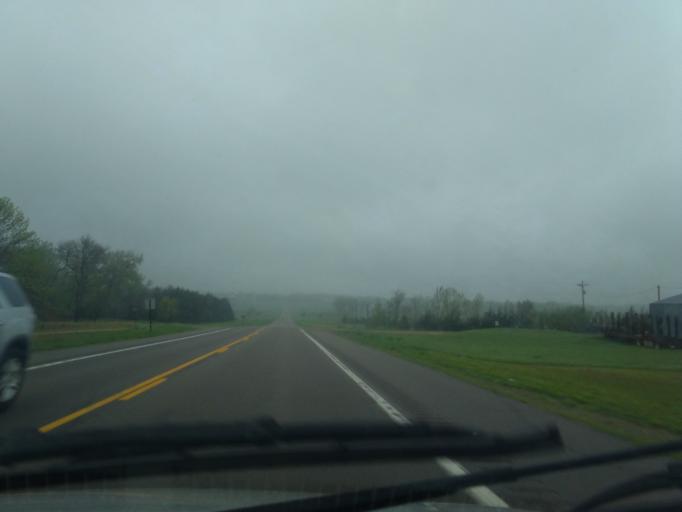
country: US
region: Nebraska
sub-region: Madison County
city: Norfolk
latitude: 42.0916
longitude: -97.3206
